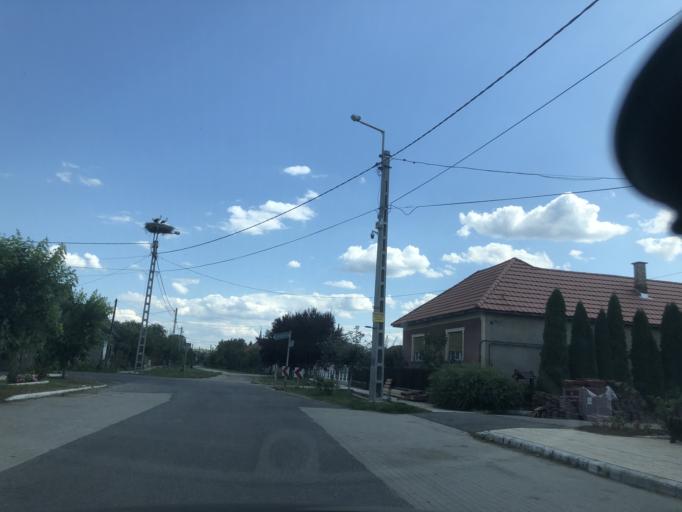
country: HU
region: Borsod-Abauj-Zemplen
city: Szendro
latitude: 48.5459
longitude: 20.7611
